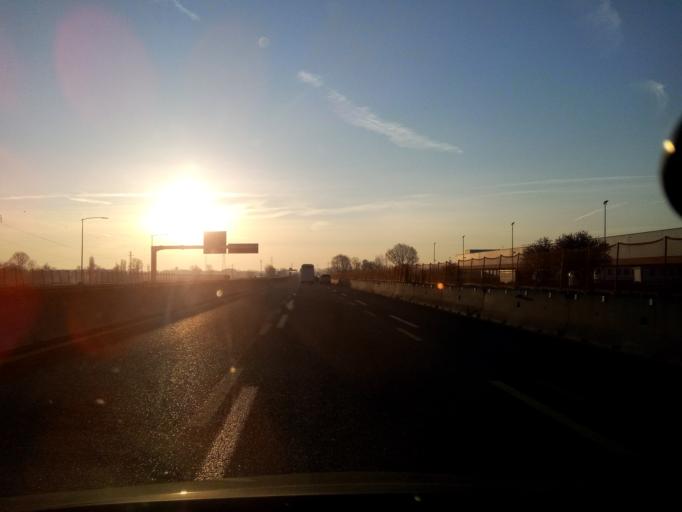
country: IT
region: Lombardy
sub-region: Citta metropolitana di Milano
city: Cerro al Lambro
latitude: 45.3376
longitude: 9.3346
